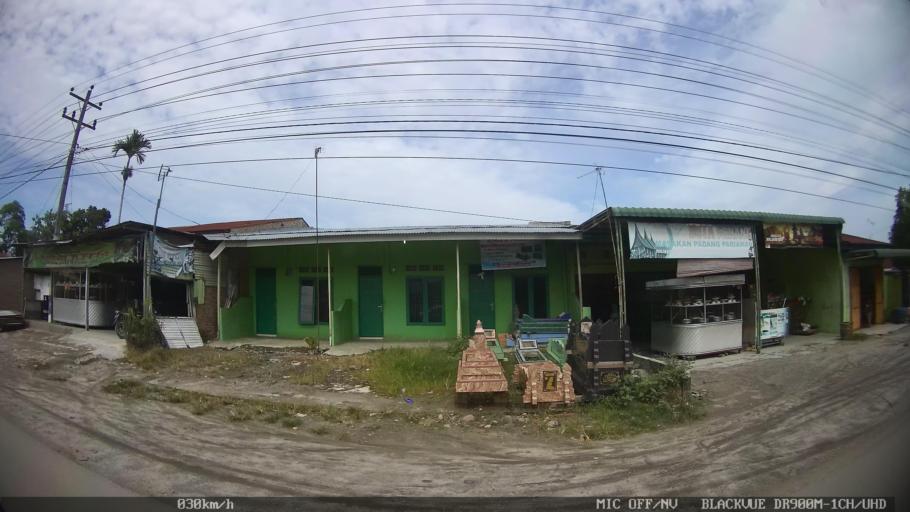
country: ID
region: North Sumatra
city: Percut
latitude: 3.6026
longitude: 98.8075
